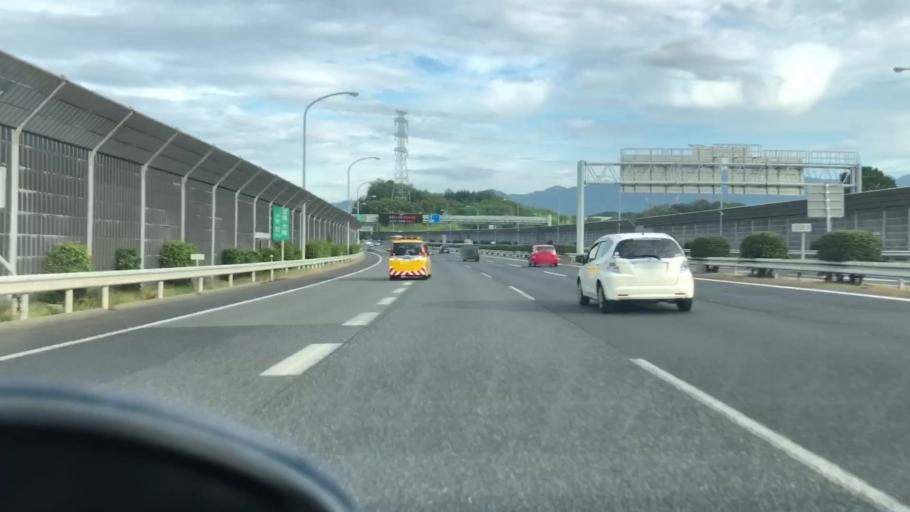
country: JP
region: Hyogo
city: Sandacho
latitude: 34.8419
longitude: 135.2285
